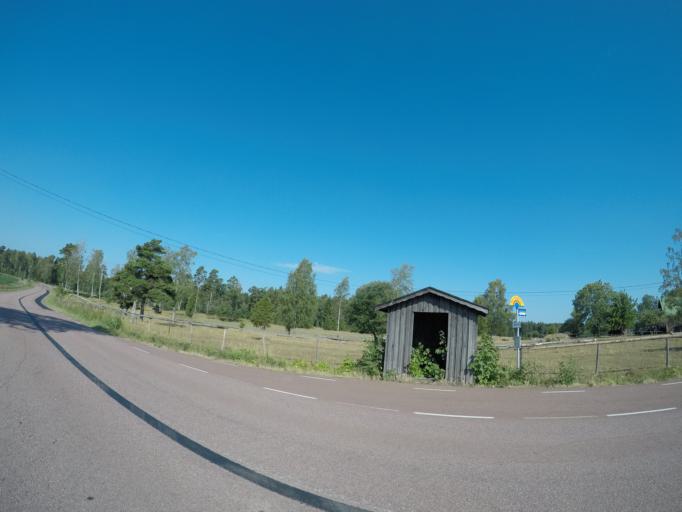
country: AX
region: Alands landsbygd
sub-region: Finstroem
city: Finstroem
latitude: 60.2804
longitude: 19.9567
